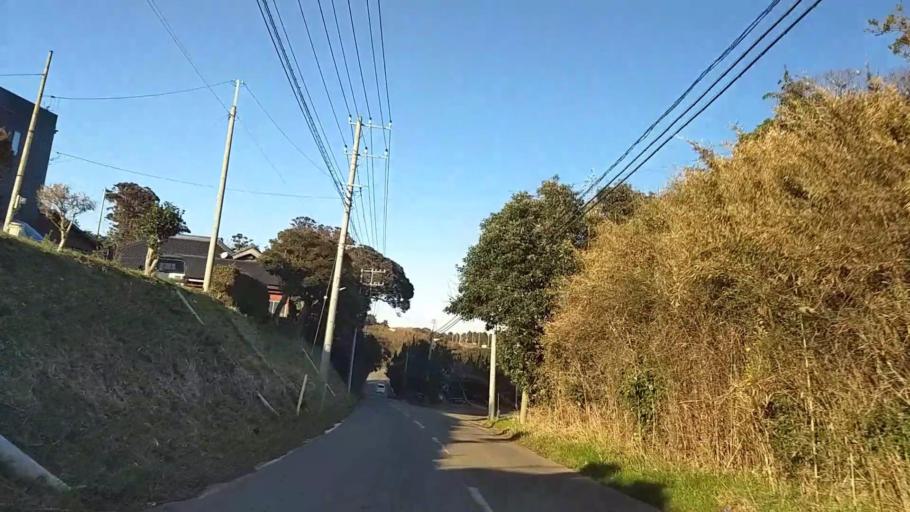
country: JP
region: Chiba
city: Asahi
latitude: 35.7235
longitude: 140.7357
